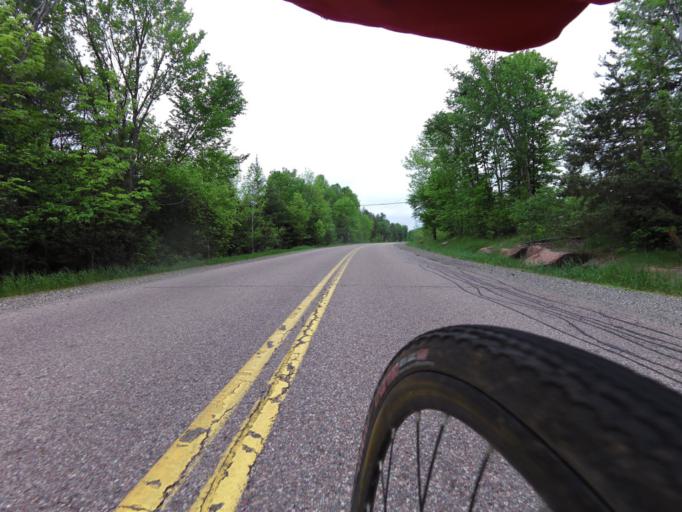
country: CA
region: Ontario
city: Renfrew
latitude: 45.2912
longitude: -76.6965
